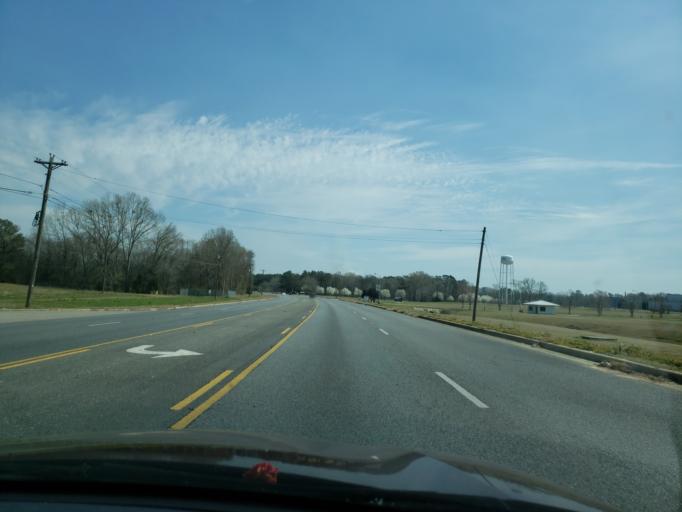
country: US
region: Alabama
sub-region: Elmore County
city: Wetumpka
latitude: 32.5355
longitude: -86.2564
